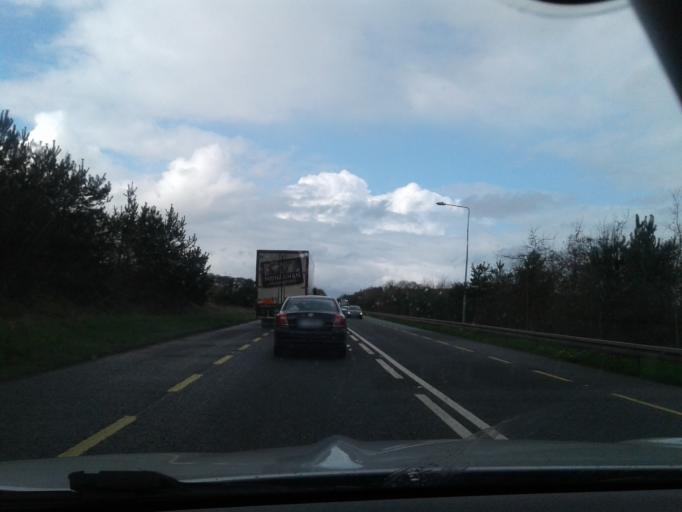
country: IE
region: Ulster
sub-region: County Monaghan
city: Carrickmacross
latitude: 53.9479
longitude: -6.6695
